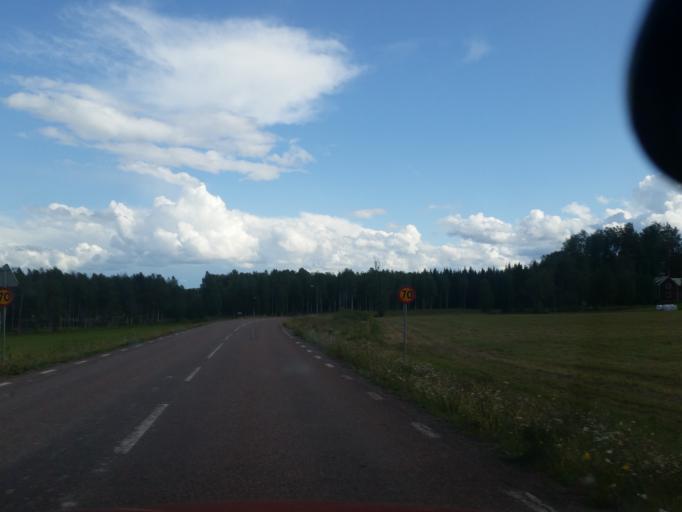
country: SE
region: Dalarna
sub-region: Gagnefs Kommun
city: Gagnef
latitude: 60.6709
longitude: 15.1462
